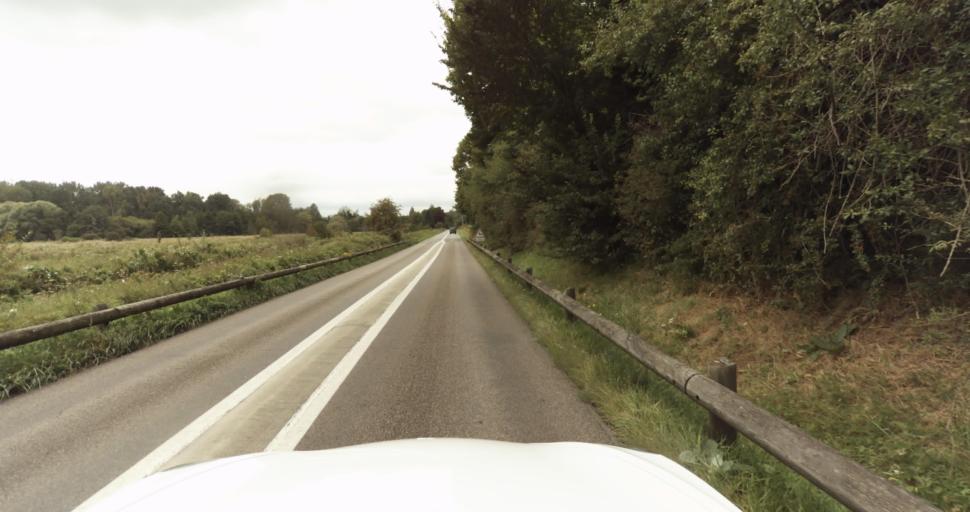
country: FR
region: Haute-Normandie
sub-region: Departement de l'Eure
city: Saint-Sebastien-de-Morsent
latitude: 48.9983
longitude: 1.0717
